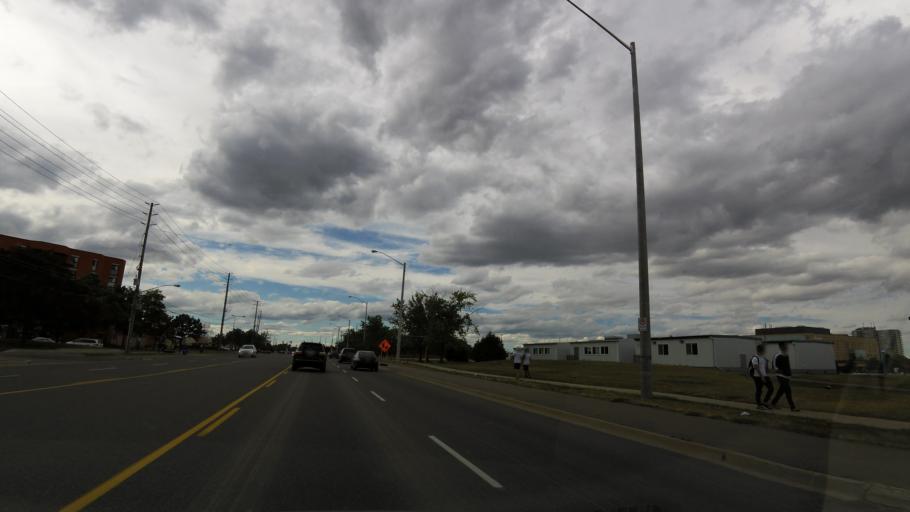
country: CA
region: Ontario
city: Brampton
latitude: 43.6546
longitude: -79.7411
